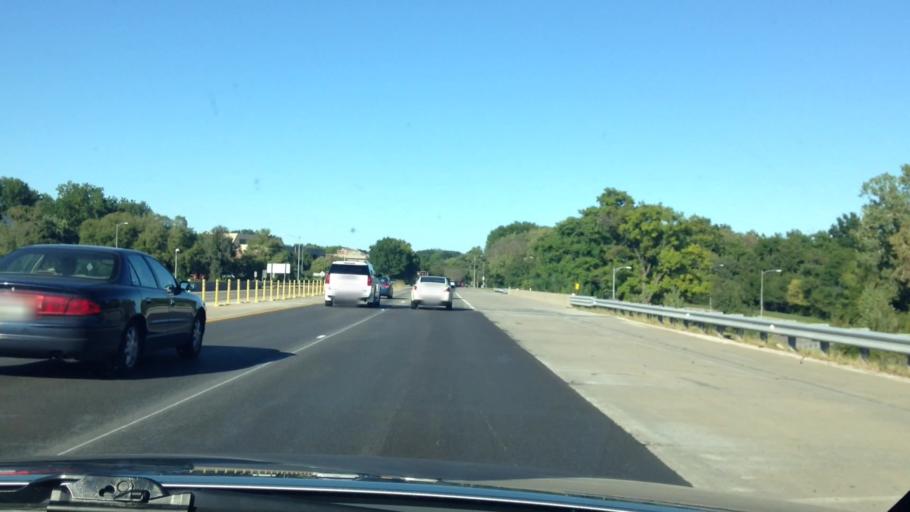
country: US
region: Kansas
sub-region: Johnson County
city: Fairway
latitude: 39.0238
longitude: -94.6390
